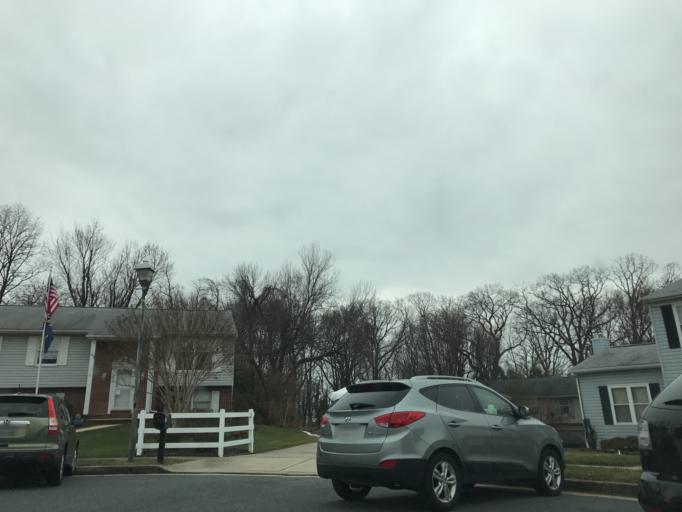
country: US
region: Maryland
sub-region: Baltimore County
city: Rossville
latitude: 39.3446
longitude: -76.4795
